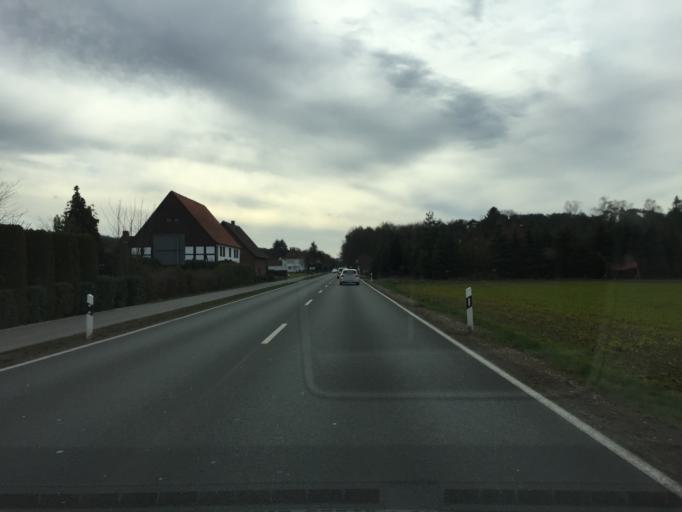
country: DE
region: North Rhine-Westphalia
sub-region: Regierungsbezirk Detmold
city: Lage
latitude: 52.0139
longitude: 8.7680
